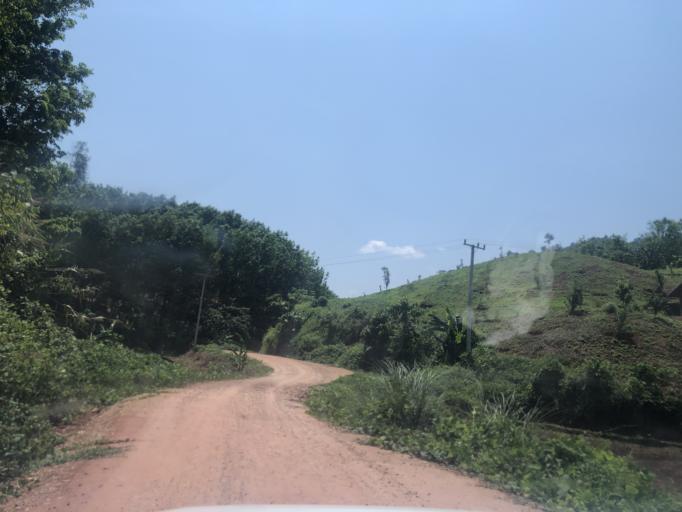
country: LA
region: Phongsali
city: Phongsali
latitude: 21.4254
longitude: 101.9865
